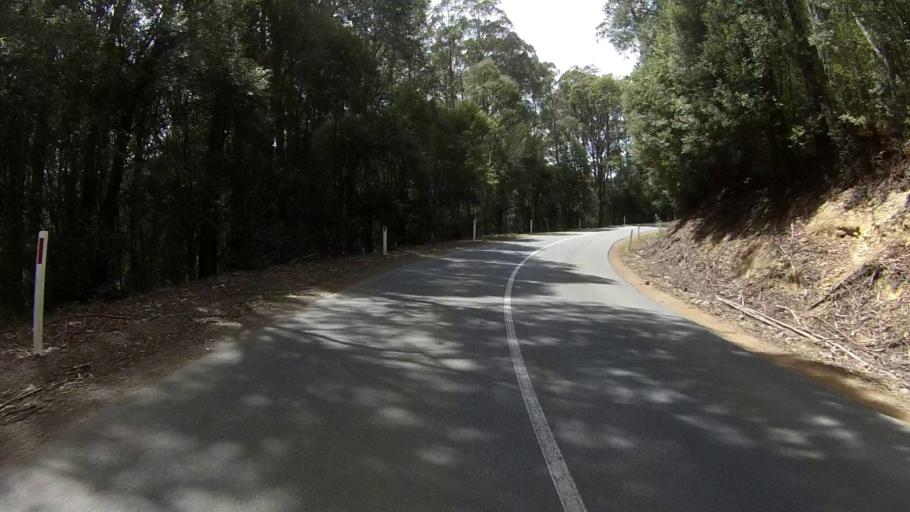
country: AU
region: Tasmania
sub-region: Kingborough
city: Kettering
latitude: -43.1262
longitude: 147.1684
